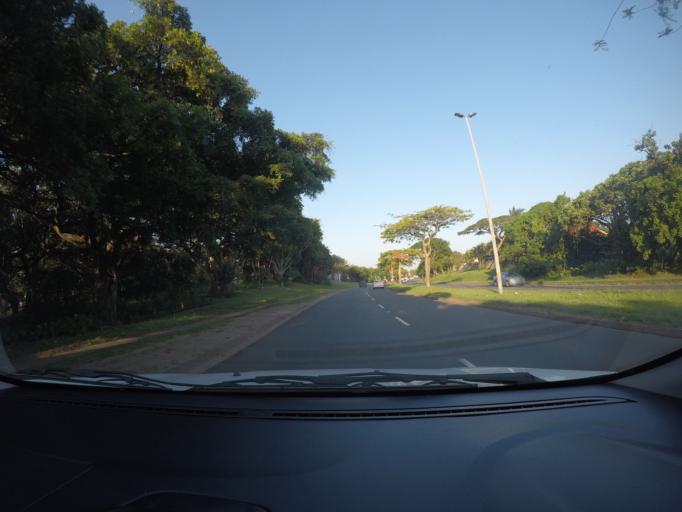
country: ZA
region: KwaZulu-Natal
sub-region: uThungulu District Municipality
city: Richards Bay
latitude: -28.7841
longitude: 32.0953
